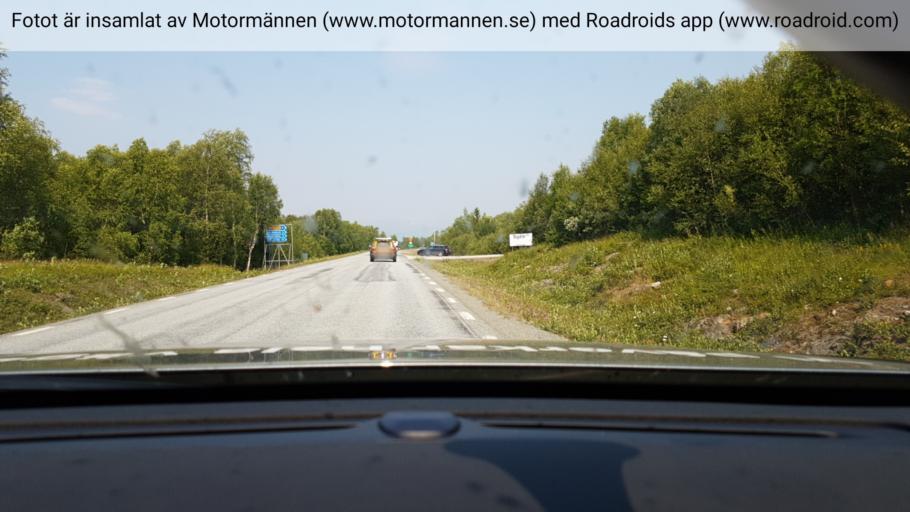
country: NO
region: Nordland
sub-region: Rana
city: Mo i Rana
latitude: 65.7826
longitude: 15.1105
